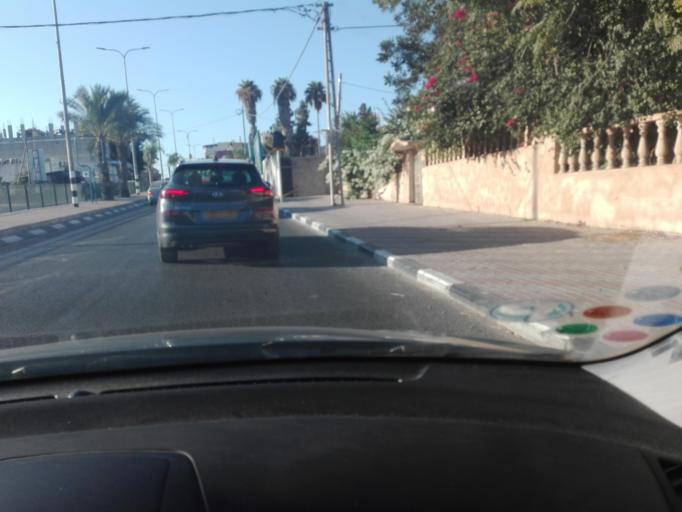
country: PS
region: West Bank
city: Nazlat `Isa
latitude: 32.4117
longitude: 35.0473
